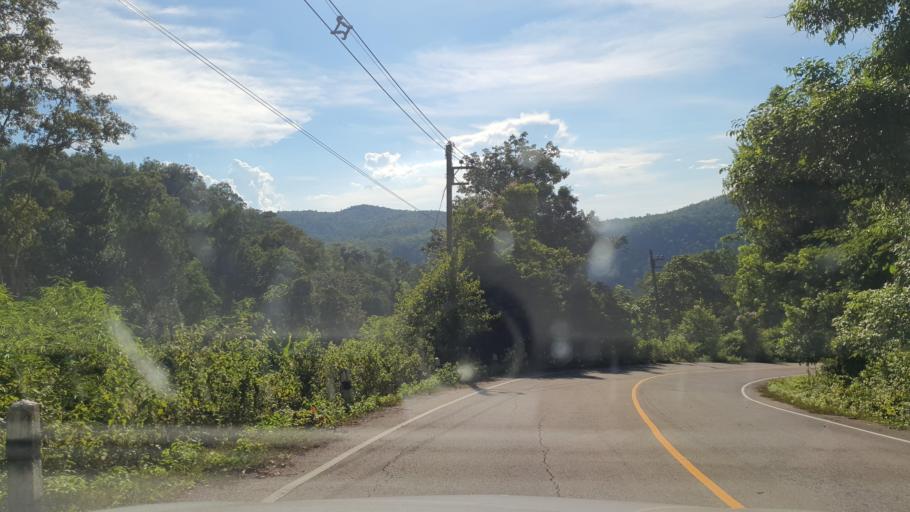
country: TH
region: Chiang Mai
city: Mae On
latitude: 18.7920
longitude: 99.3063
